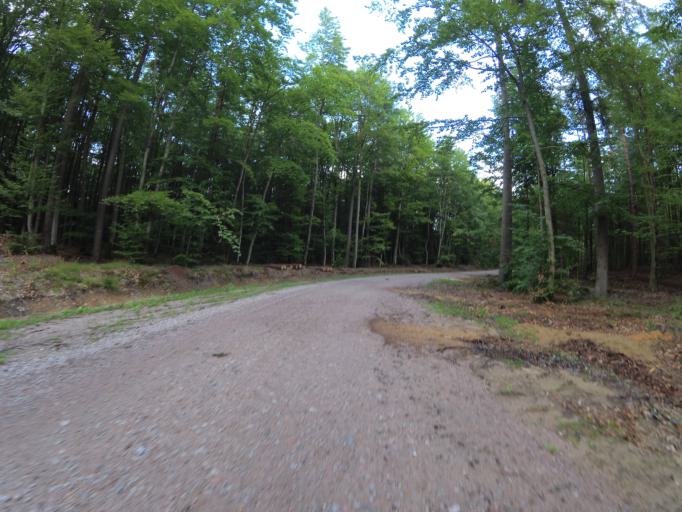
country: PL
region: Pomeranian Voivodeship
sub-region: Powiat wejherowski
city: Bojano
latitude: 54.5087
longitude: 18.4196
